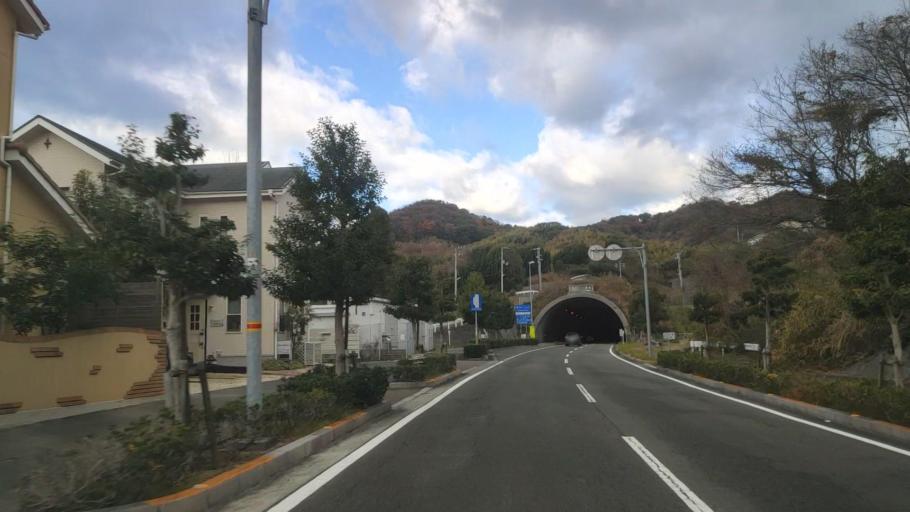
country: JP
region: Ehime
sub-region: Shikoku-chuo Shi
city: Matsuyama
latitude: 33.8752
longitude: 132.7150
